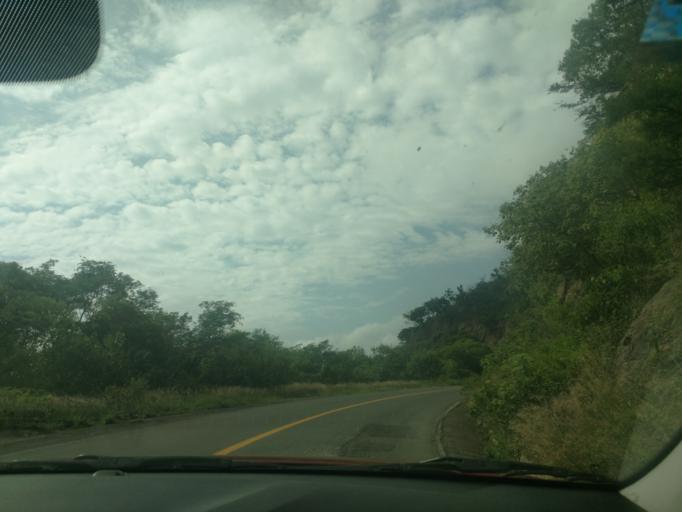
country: MX
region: Jalisco
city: El Salto
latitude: 20.3656
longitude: -104.5833
